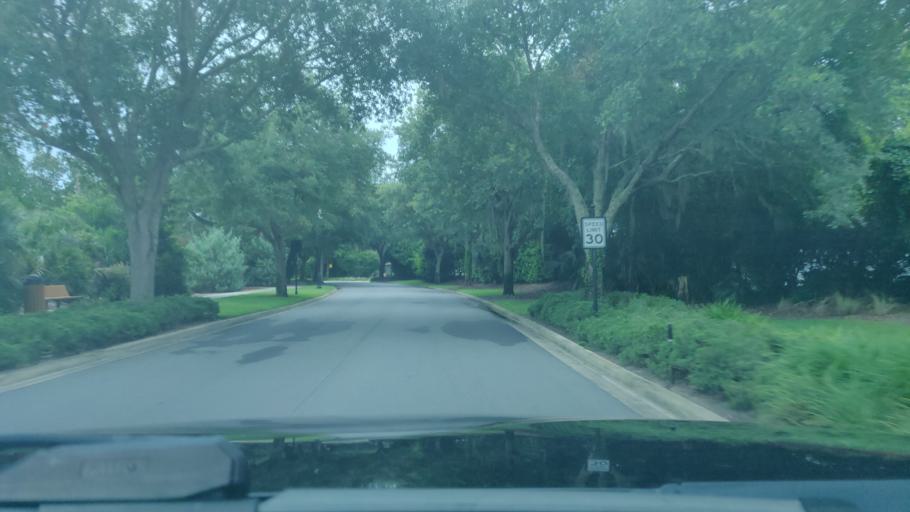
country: US
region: Florida
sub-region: Flagler County
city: Palm Coast
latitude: 29.5401
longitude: -81.1725
